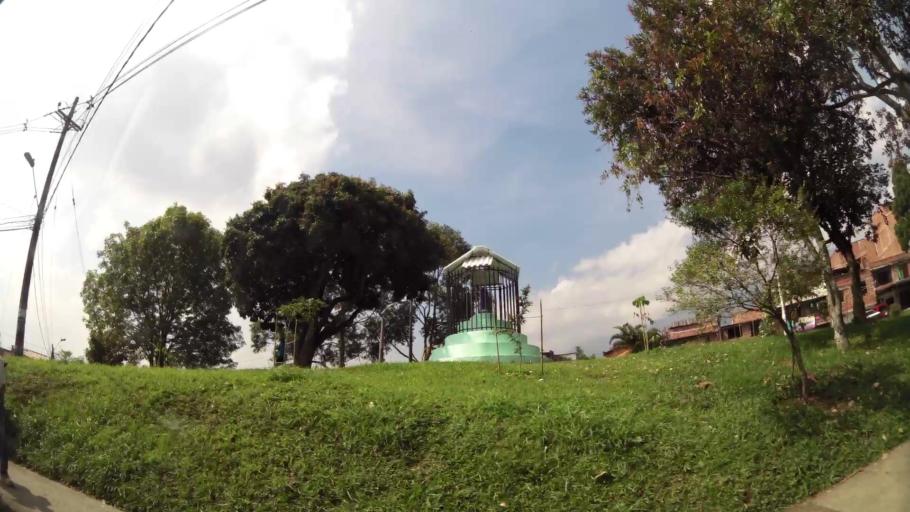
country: CO
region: Antioquia
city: La Estrella
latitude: 6.1783
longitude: -75.6432
